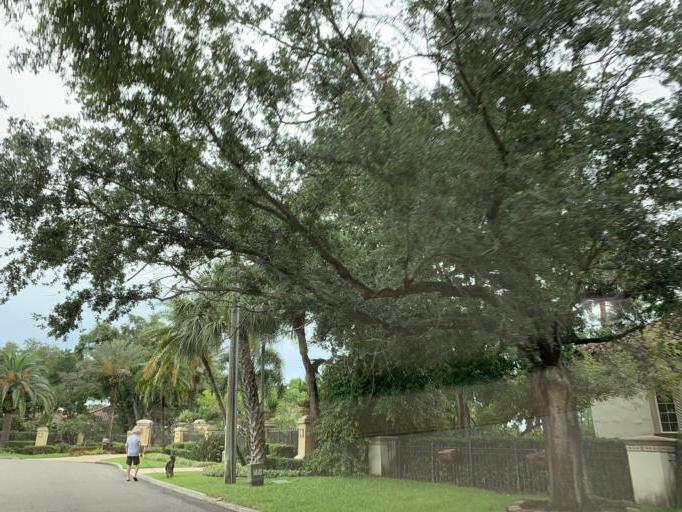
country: US
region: Florida
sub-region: Pinellas County
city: Gandy
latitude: 27.7975
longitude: -82.6075
